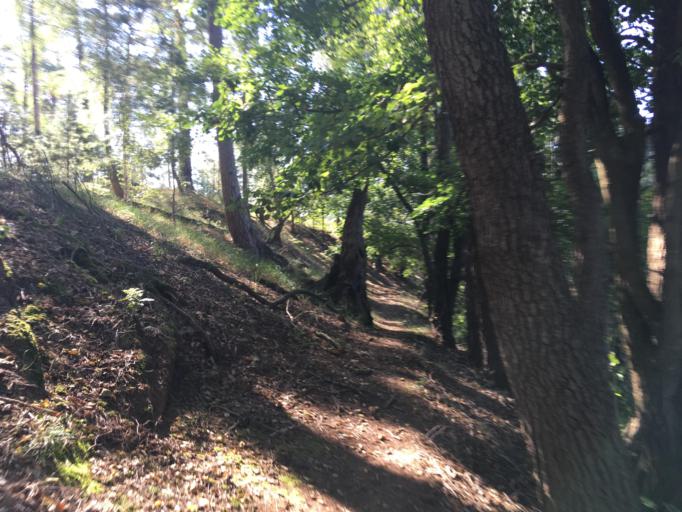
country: DE
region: Brandenburg
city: Gross Koris
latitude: 52.2083
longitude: 13.7490
